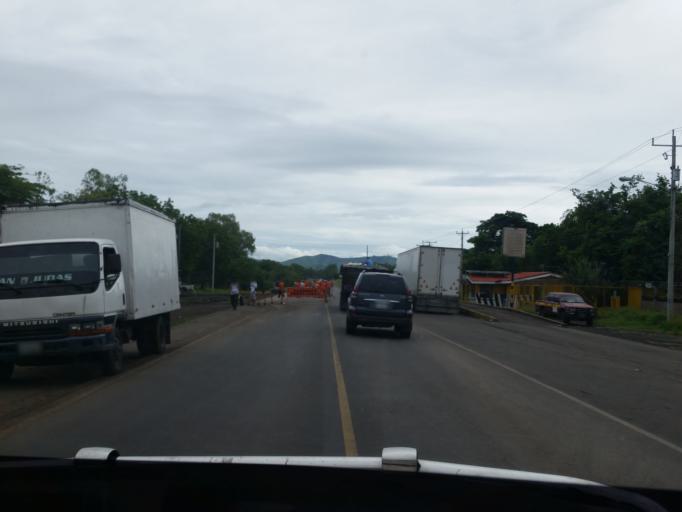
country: NI
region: Managua
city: Tipitapa
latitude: 12.2812
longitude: -86.0639
